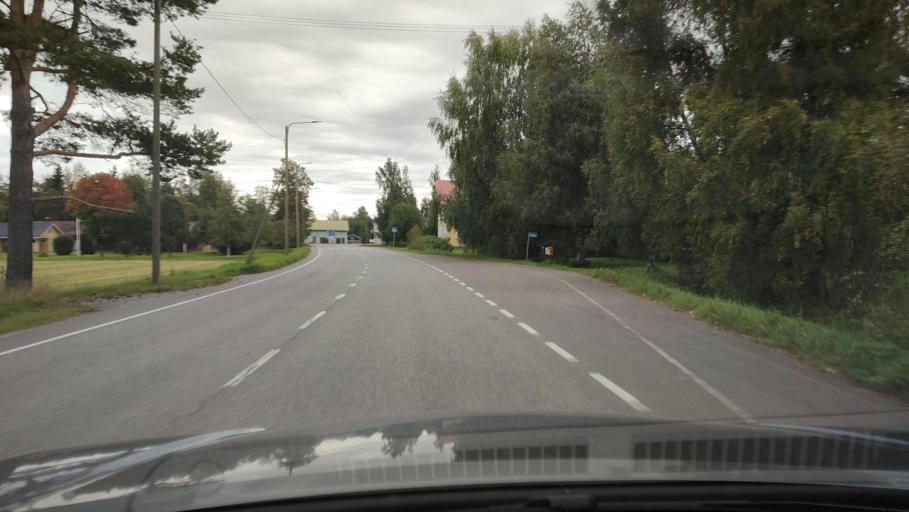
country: FI
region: Ostrobothnia
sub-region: Sydosterbotten
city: Kristinestad
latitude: 62.2576
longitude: 21.5239
